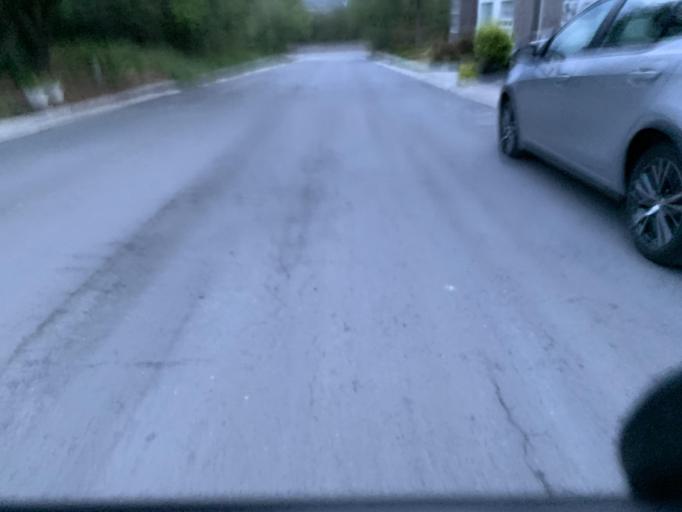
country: MX
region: Nuevo Leon
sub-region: Juarez
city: Bosques de San Pedro
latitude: 25.5109
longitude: -100.1868
